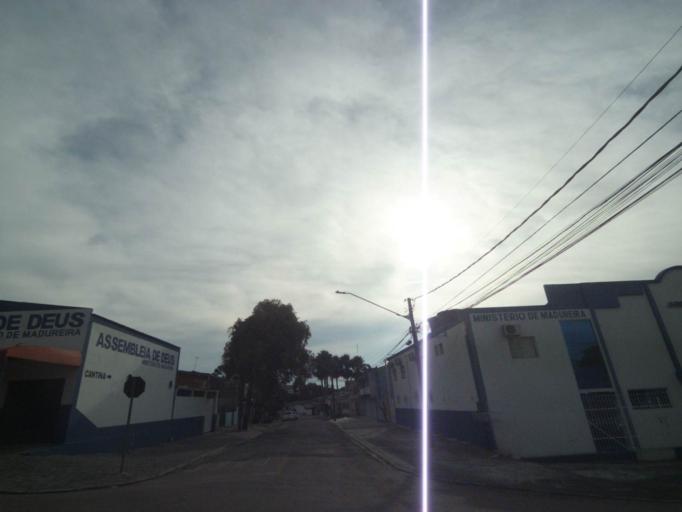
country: BR
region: Parana
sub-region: Pinhais
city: Pinhais
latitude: -25.4504
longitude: -49.2218
